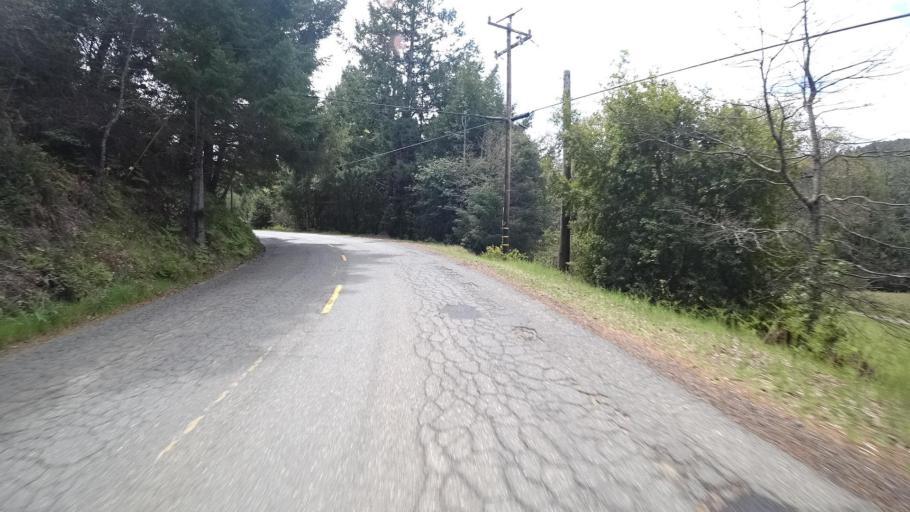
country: US
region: California
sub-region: Humboldt County
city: Redway
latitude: 40.0471
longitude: -123.9614
